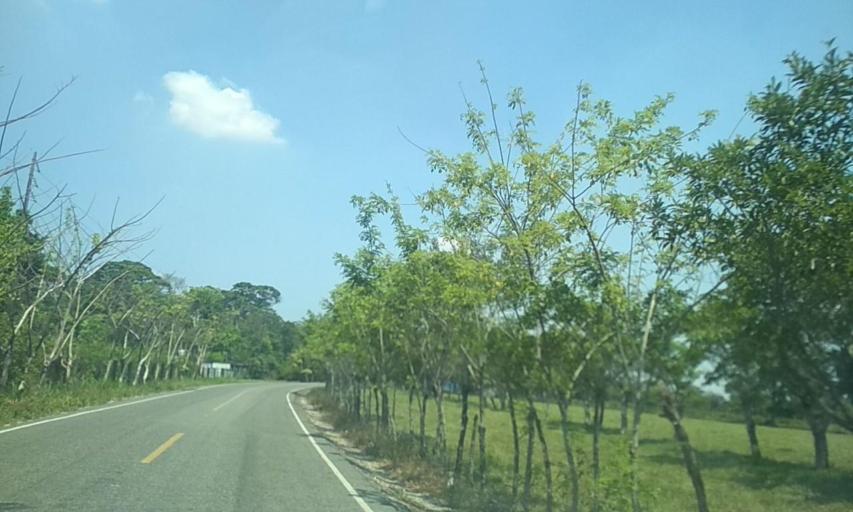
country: MX
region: Tabasco
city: Huimanguillo
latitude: 17.8017
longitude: -93.4876
